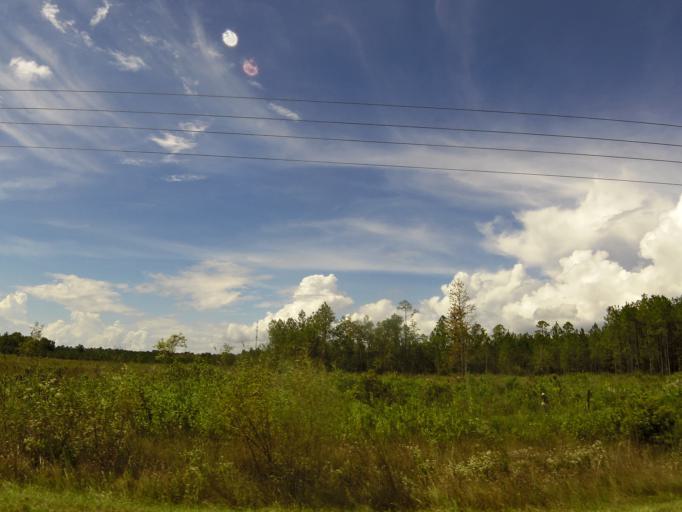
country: US
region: Florida
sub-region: Union County
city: Lake Butler
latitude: 30.0127
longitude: -82.3138
